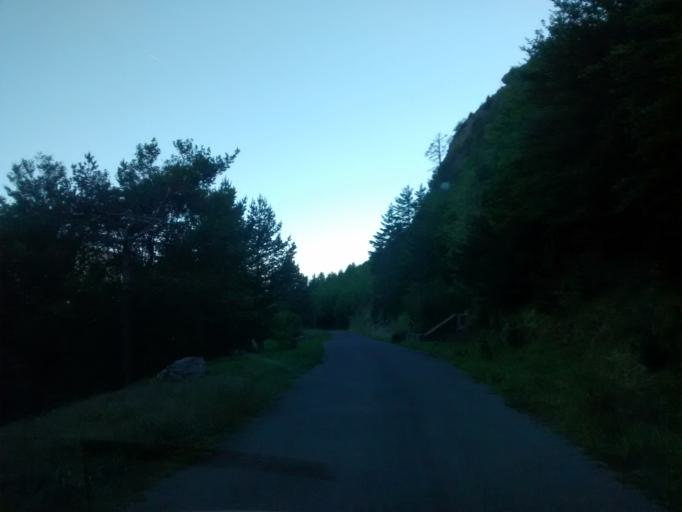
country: ES
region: Aragon
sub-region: Provincia de Huesca
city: Canfranc
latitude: 42.7347
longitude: -0.5942
